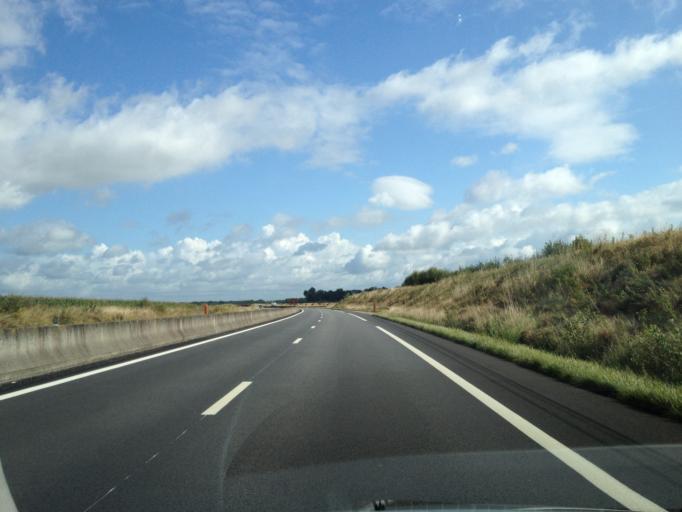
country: FR
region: Haute-Normandie
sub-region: Departement de l'Eure
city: Bourg-Achard
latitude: 49.3140
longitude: 0.8196
